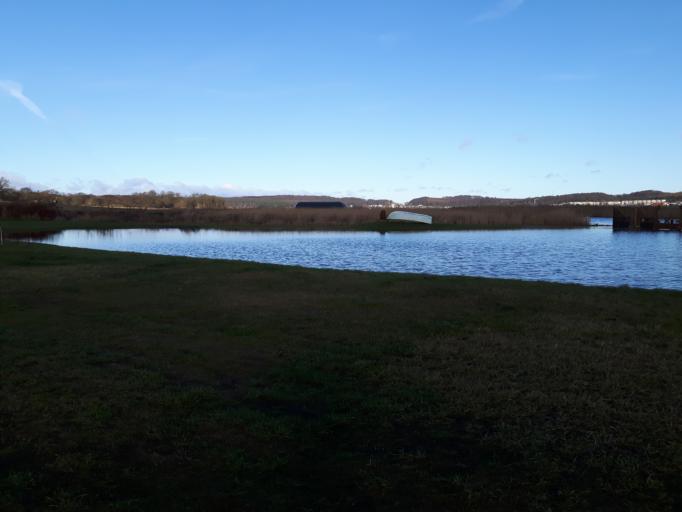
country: DE
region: Mecklenburg-Vorpommern
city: Ostseebad Sellin
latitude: 54.3528
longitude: 13.6854
